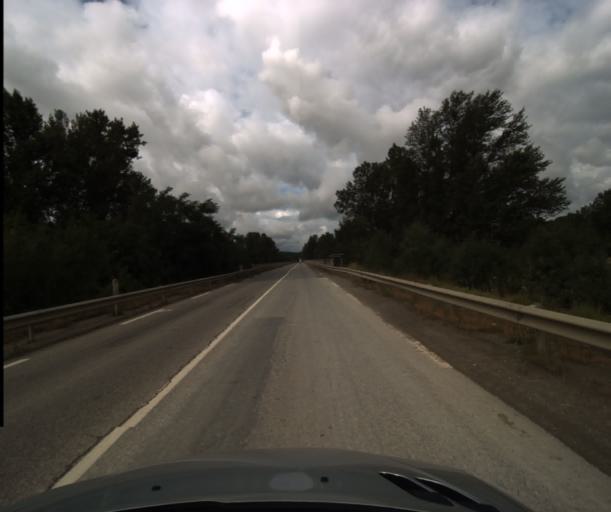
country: FR
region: Midi-Pyrenees
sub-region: Departement du Tarn-et-Garonne
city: Castelsarrasin
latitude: 44.0235
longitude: 1.0808
